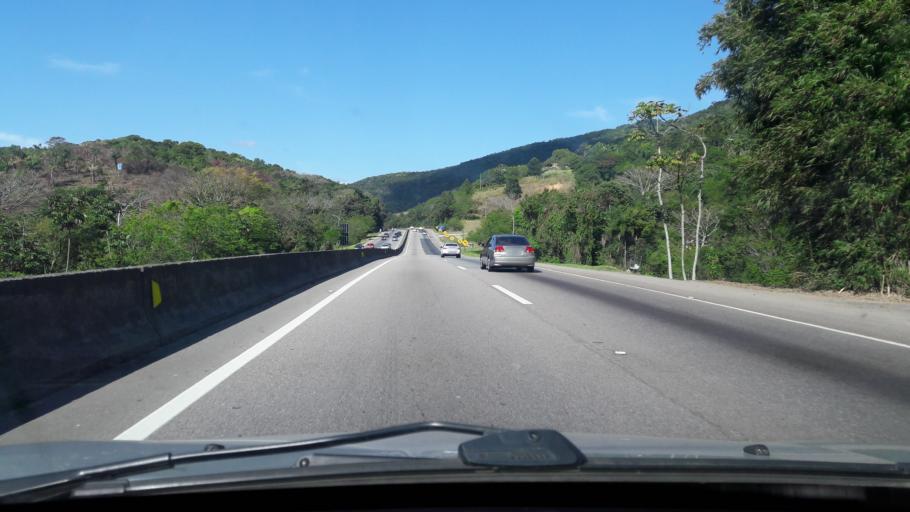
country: BR
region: Santa Catarina
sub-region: Biguacu
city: Biguacu
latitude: -27.4609
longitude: -48.6399
